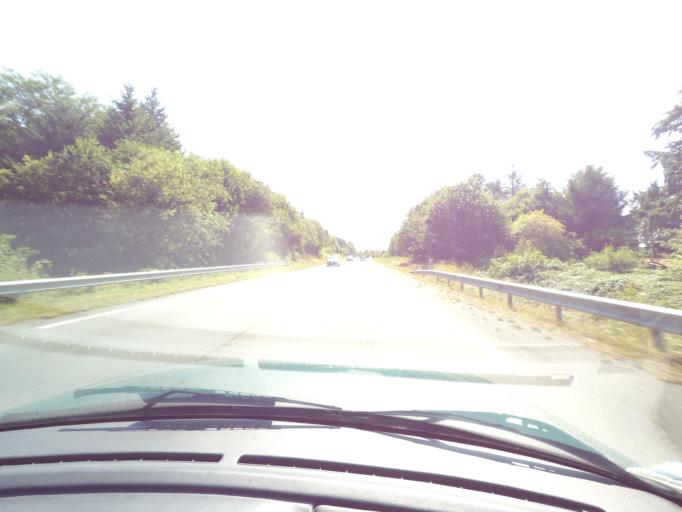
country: FR
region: Limousin
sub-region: Departement de la Haute-Vienne
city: Chaptelat
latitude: 45.8995
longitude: 1.2378
